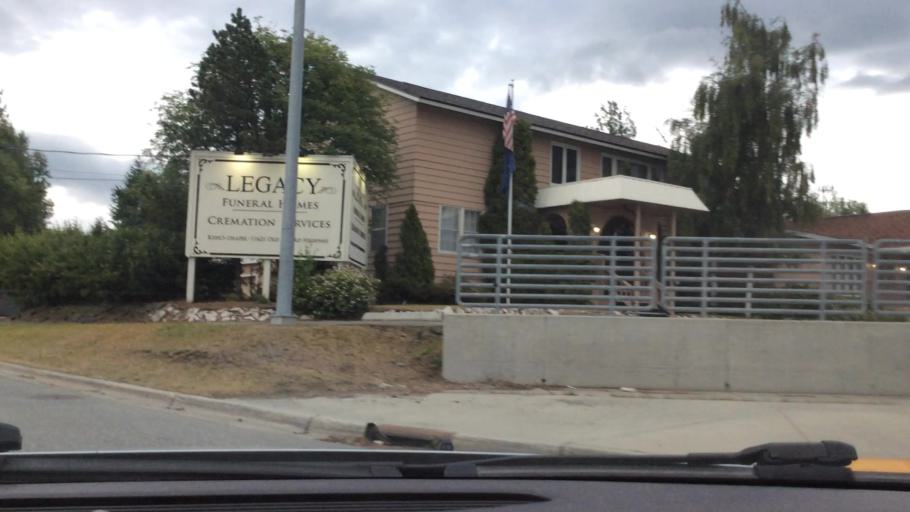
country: US
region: Alaska
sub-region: Anchorage Municipality
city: Anchorage
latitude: 61.1159
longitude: -149.8636
